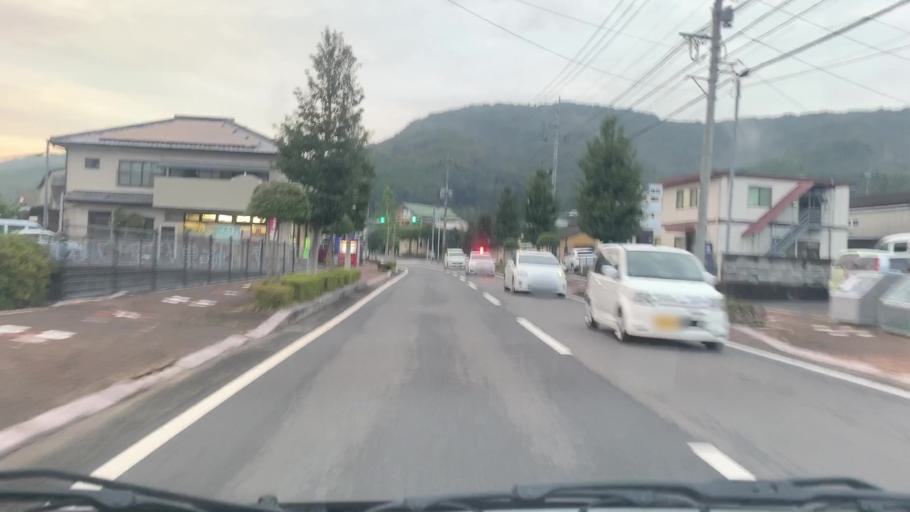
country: JP
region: Saga Prefecture
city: Ureshinomachi-shimojuku
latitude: 33.1489
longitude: 129.9006
